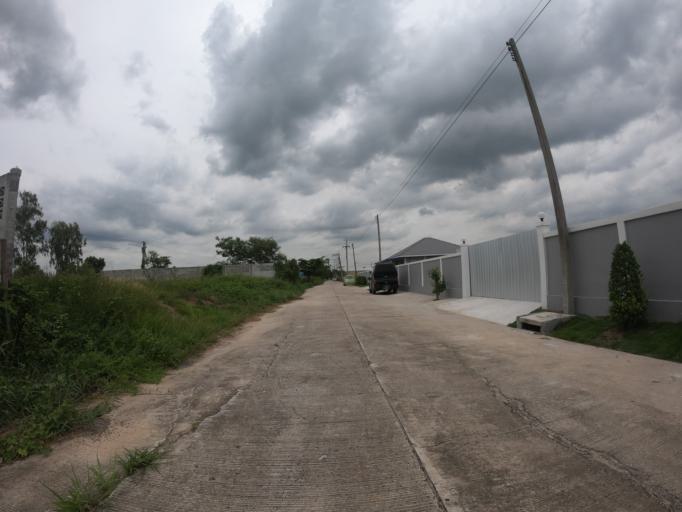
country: TH
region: Pathum Thani
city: Nong Suea
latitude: 14.0482
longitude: 100.8467
